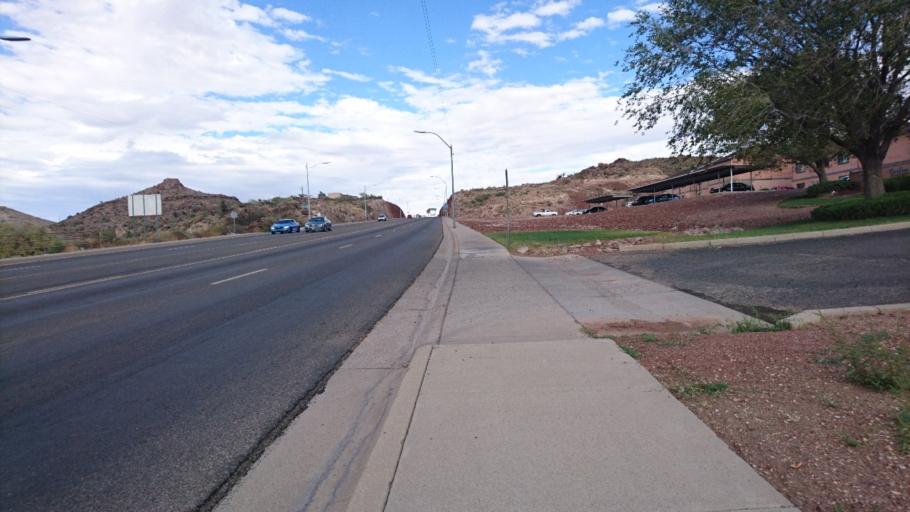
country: US
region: Arizona
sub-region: Mohave County
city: Kingman
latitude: 35.1873
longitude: -114.0389
